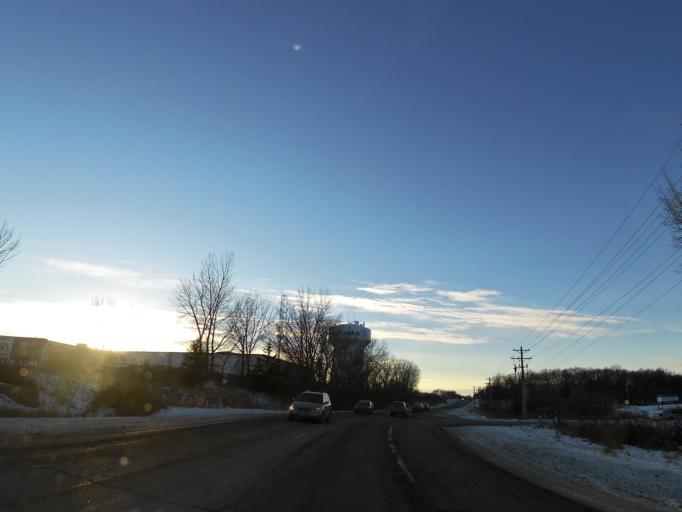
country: US
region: Minnesota
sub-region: Hennepin County
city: Shorewood
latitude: 44.8490
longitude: -93.5881
